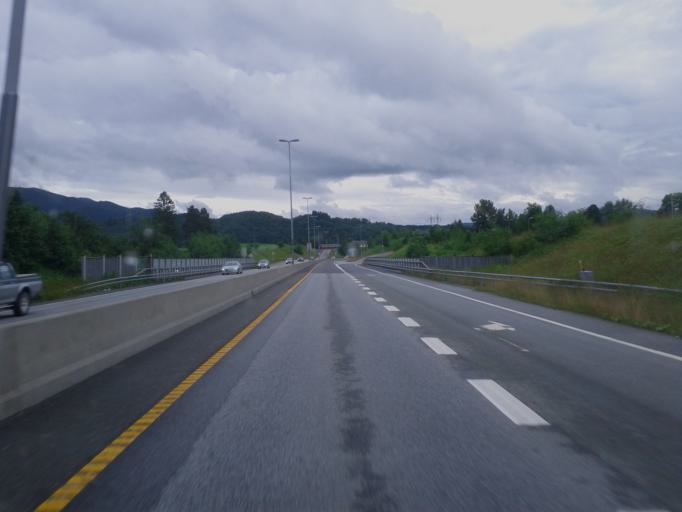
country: NO
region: Sor-Trondelag
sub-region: Melhus
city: Melhus
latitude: 63.3034
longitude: 10.2879
